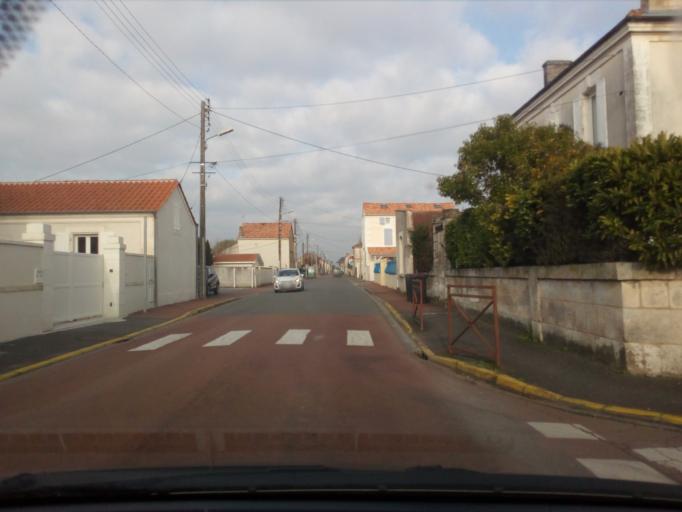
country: FR
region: Poitou-Charentes
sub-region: Departement de la Charente
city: Gond-Pontouvre
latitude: 45.6757
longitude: 0.1583
